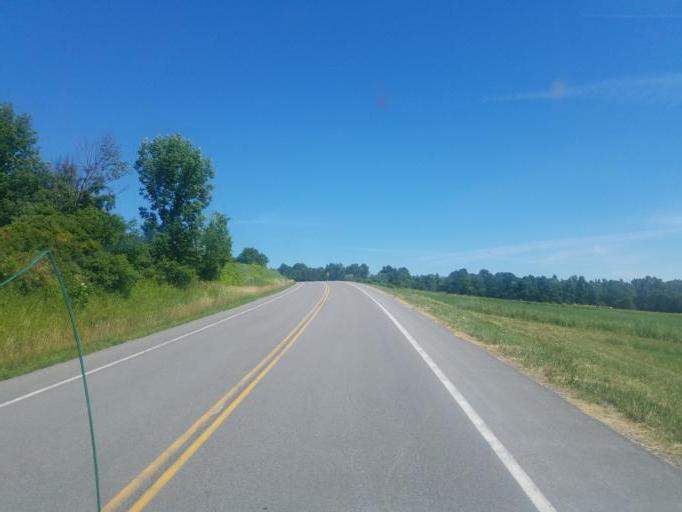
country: US
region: New York
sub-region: Ontario County
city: Canandaigua
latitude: 42.7162
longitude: -77.2757
